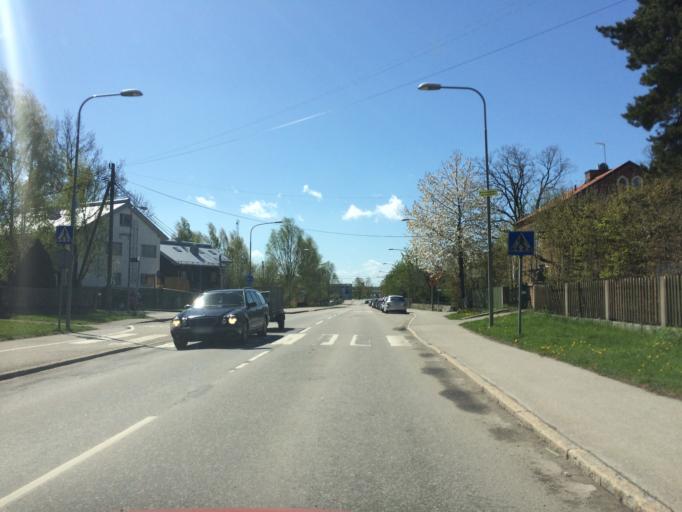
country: SE
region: Stockholm
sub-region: Huddinge Kommun
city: Segeltorp
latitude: 59.2927
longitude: 17.9525
